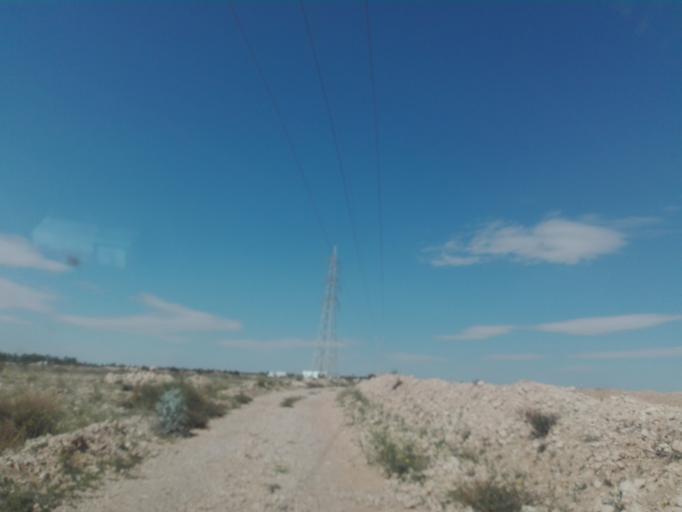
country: TN
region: Safaqis
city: Sfax
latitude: 34.6881
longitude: 10.5361
